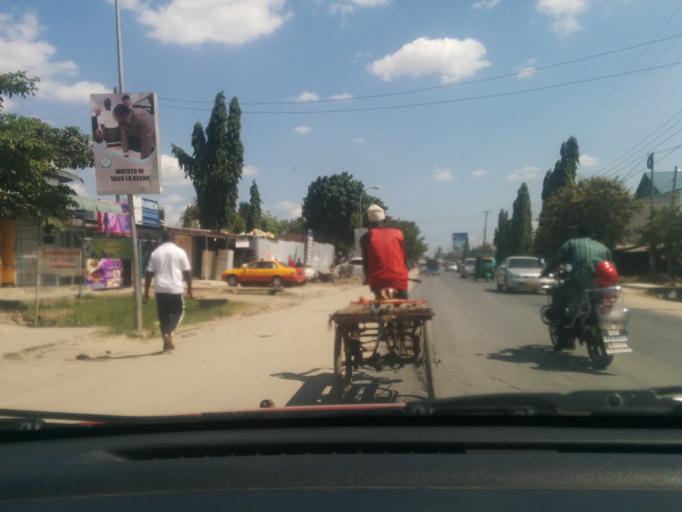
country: TZ
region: Dar es Salaam
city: Magomeni
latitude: -6.7793
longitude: 39.2258
